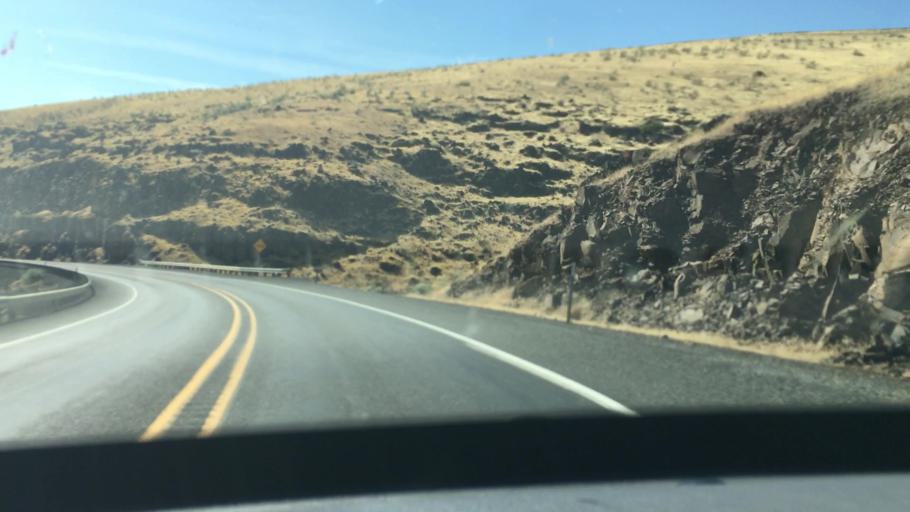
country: US
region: Washington
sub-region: Klickitat County
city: Goldendale
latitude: 45.6477
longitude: -120.7961
